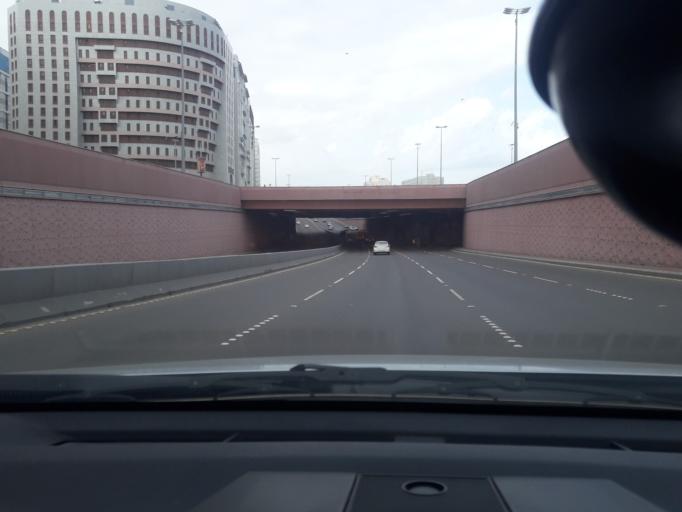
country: SA
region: Al Madinah al Munawwarah
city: Medina
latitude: 24.4741
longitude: 39.6126
